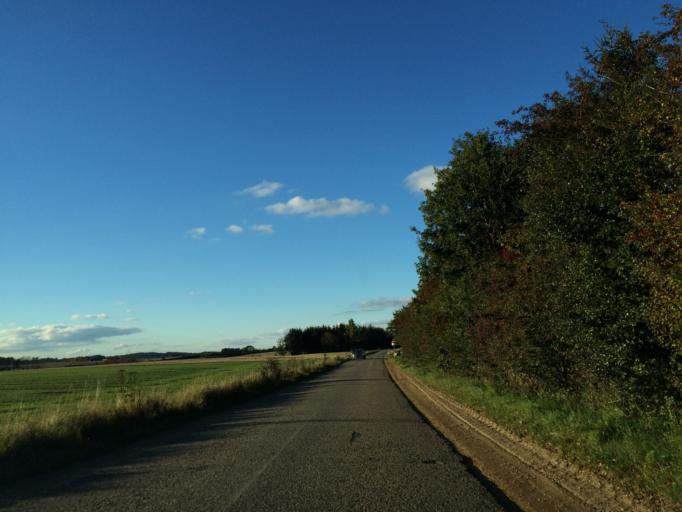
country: DK
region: Central Jutland
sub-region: Skanderborg Kommune
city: Ry
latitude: 56.1366
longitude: 9.7172
